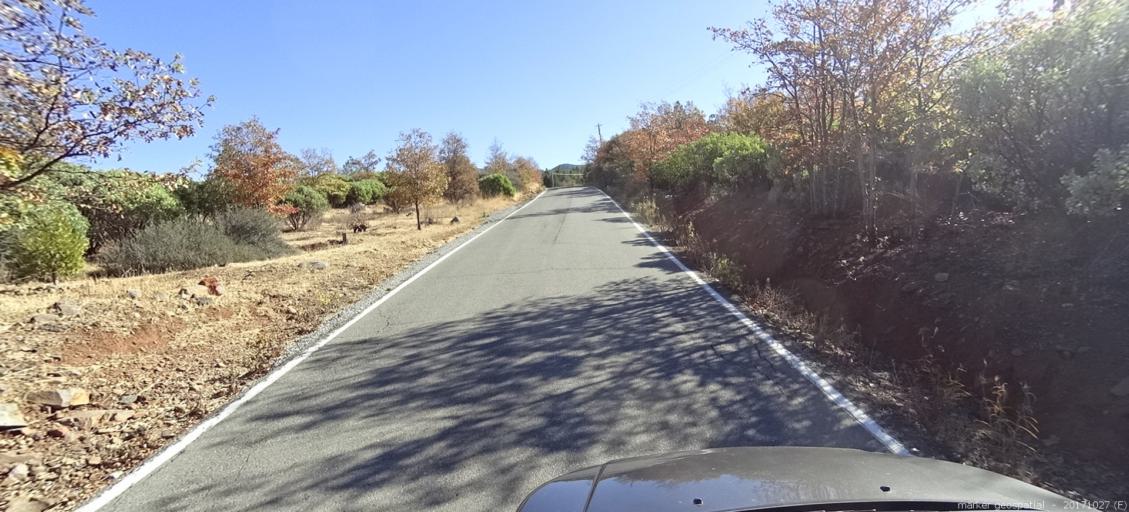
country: US
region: California
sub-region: Shasta County
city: Burney
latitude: 40.7912
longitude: -121.9232
